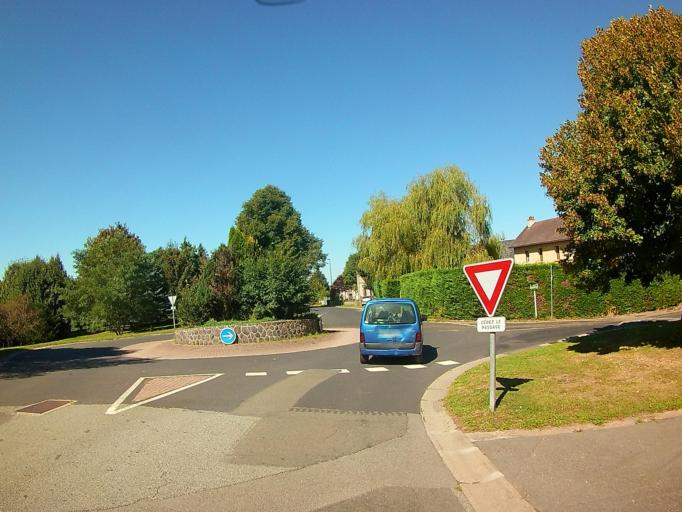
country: FR
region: Auvergne
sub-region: Departement du Puy-de-Dome
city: Saint-Ours
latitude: 45.8864
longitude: 2.9085
